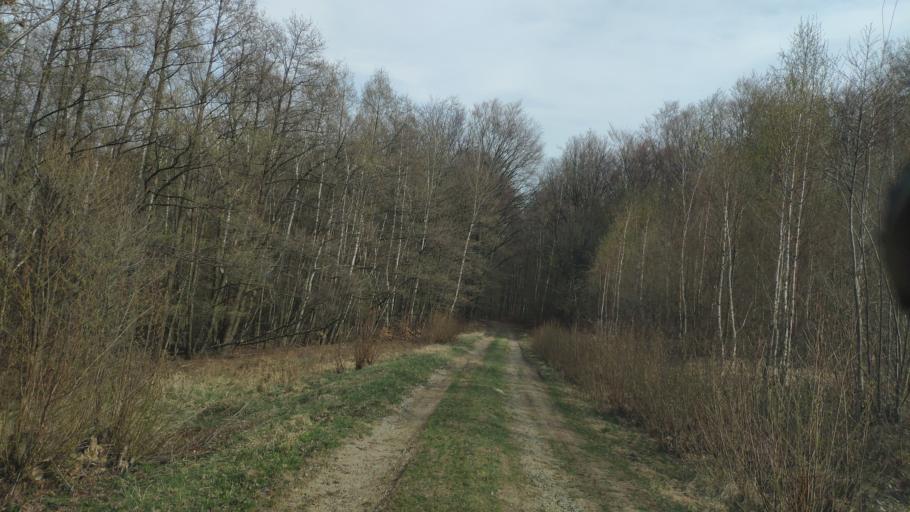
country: SK
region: Kosicky
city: Moldava nad Bodvou
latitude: 48.7352
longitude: 21.0588
